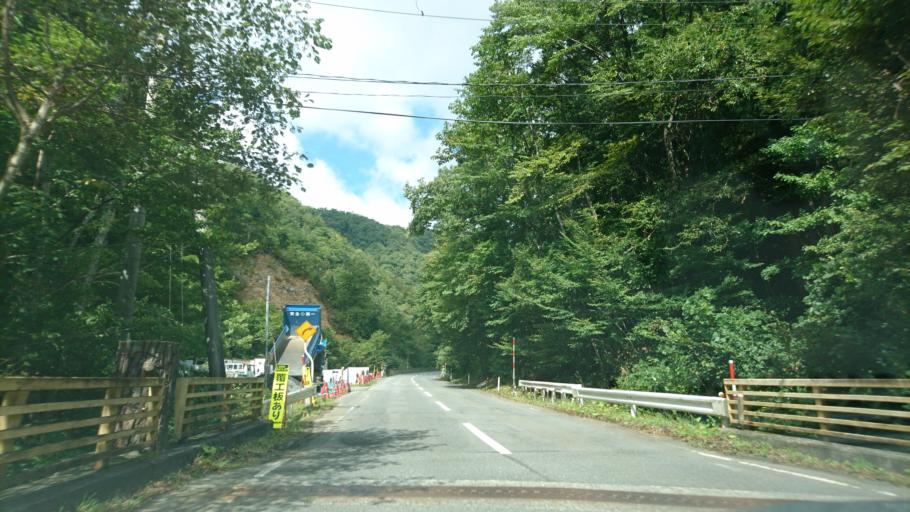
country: JP
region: Miyagi
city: Furukawa
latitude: 38.8564
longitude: 140.7804
